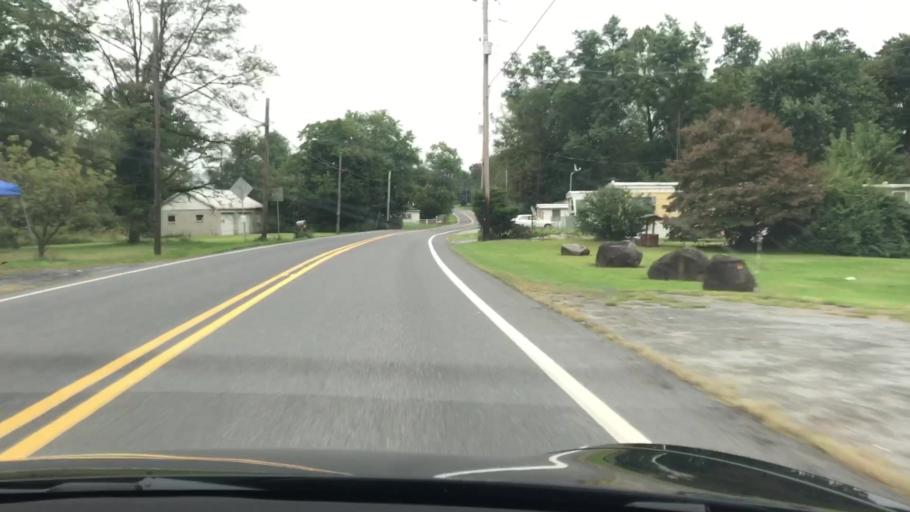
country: US
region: Pennsylvania
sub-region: Adams County
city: Lake Meade
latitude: 39.9506
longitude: -77.1148
